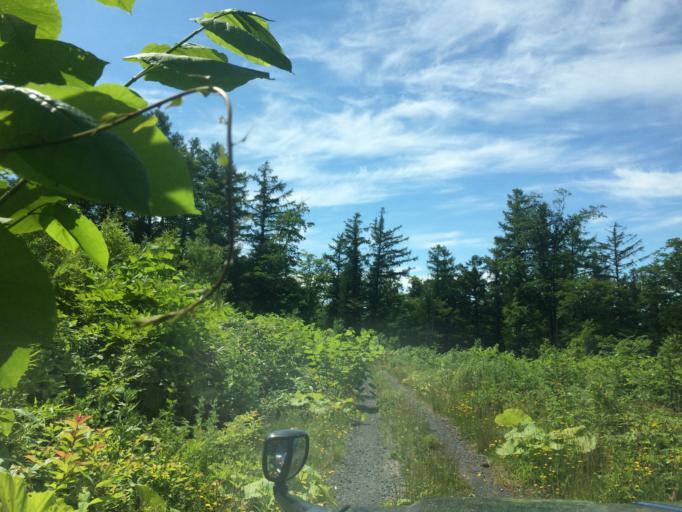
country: JP
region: Hokkaido
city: Niseko Town
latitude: 42.8654
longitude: 140.7962
